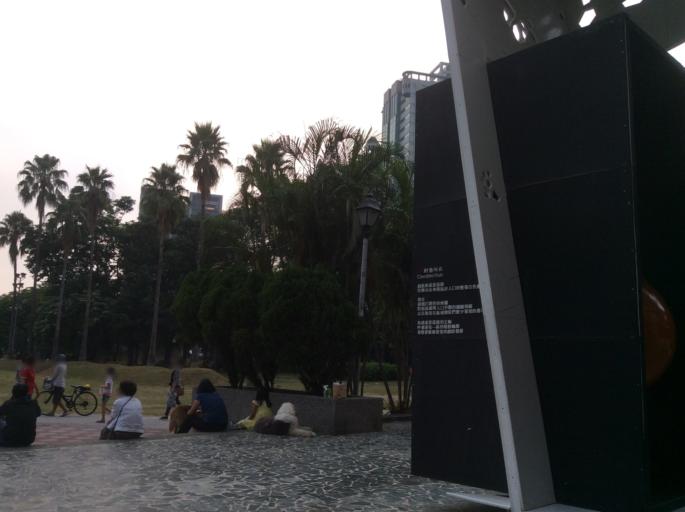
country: TW
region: Kaohsiung
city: Kaohsiung
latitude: 22.6075
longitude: 120.3095
